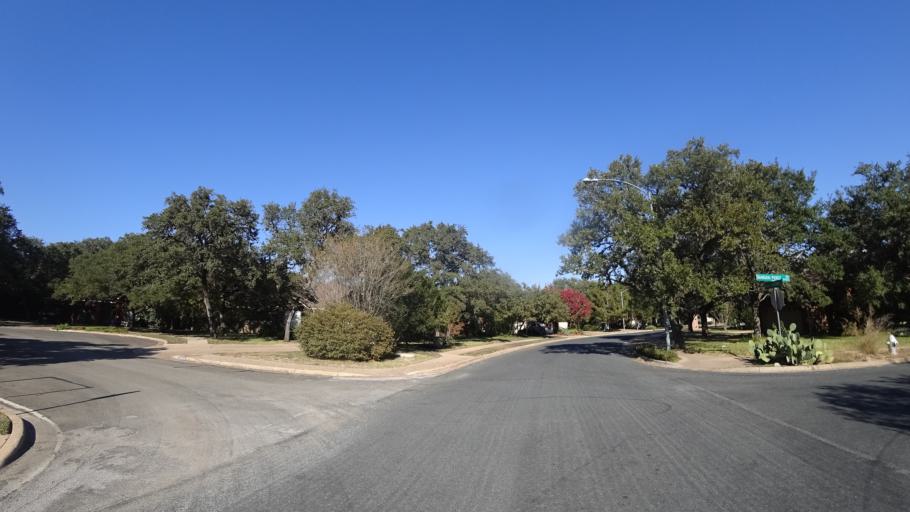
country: US
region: Texas
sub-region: Travis County
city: Shady Hollow
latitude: 30.2248
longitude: -97.8657
